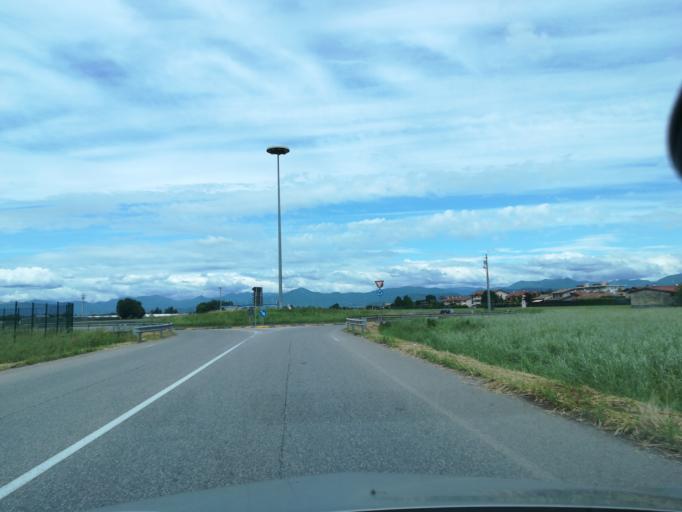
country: IT
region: Lombardy
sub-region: Provincia di Bergamo
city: Cividate al Piano
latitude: 45.5546
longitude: 9.8225
